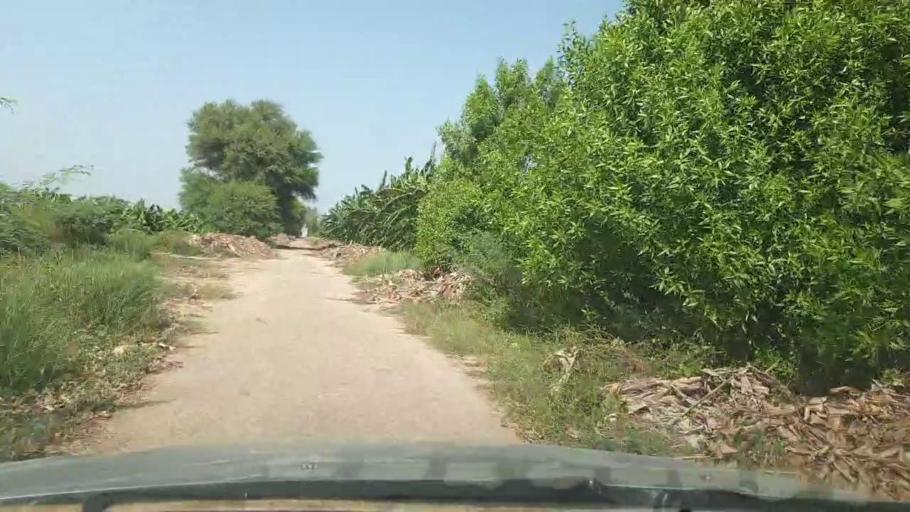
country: PK
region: Sindh
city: Tando Ghulam Ali
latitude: 25.1463
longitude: 68.8860
